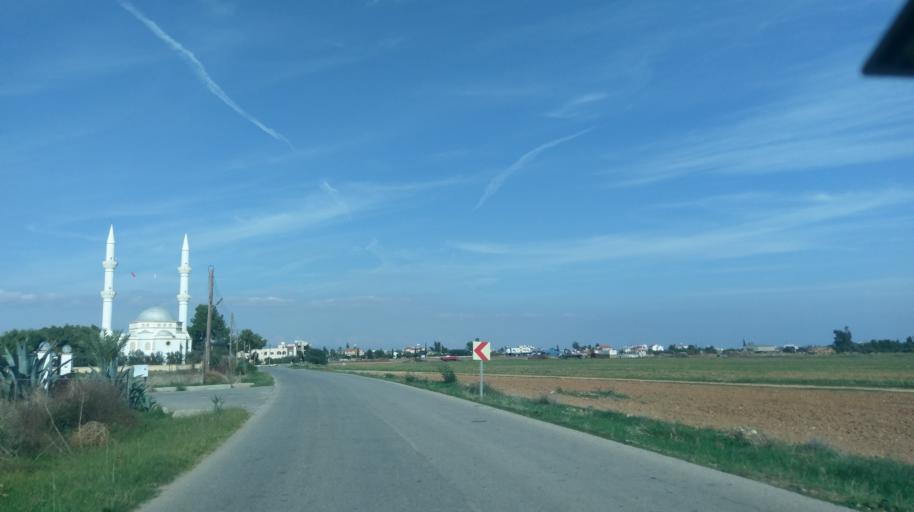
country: CY
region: Ammochostos
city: Acheritou
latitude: 35.1922
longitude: 33.8556
